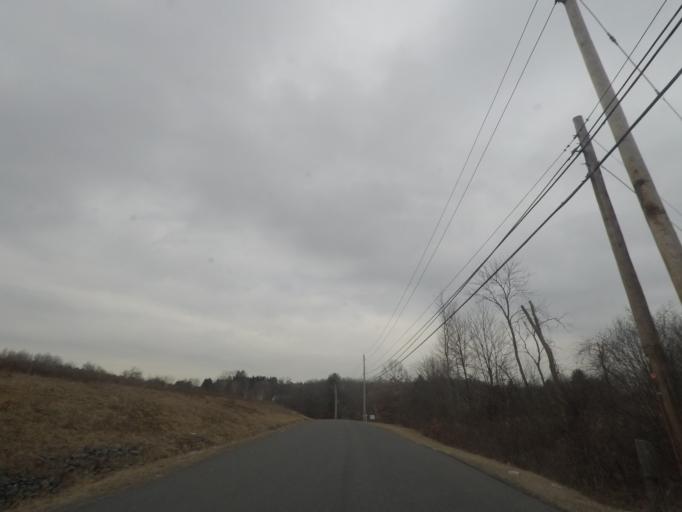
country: US
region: New York
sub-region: Rensselaer County
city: East Greenbush
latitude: 42.5700
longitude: -73.6618
